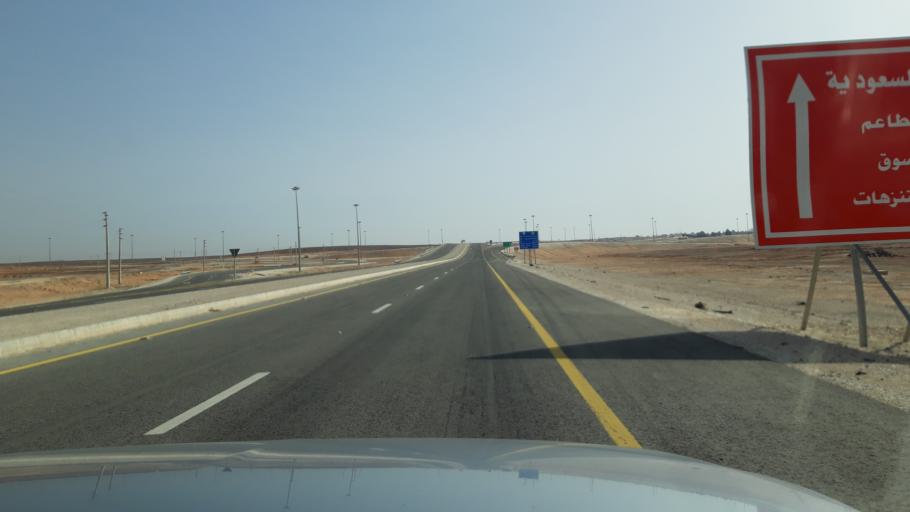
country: JO
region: Amman
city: Al Azraq ash Shamali
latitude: 31.8712
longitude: 36.7303
